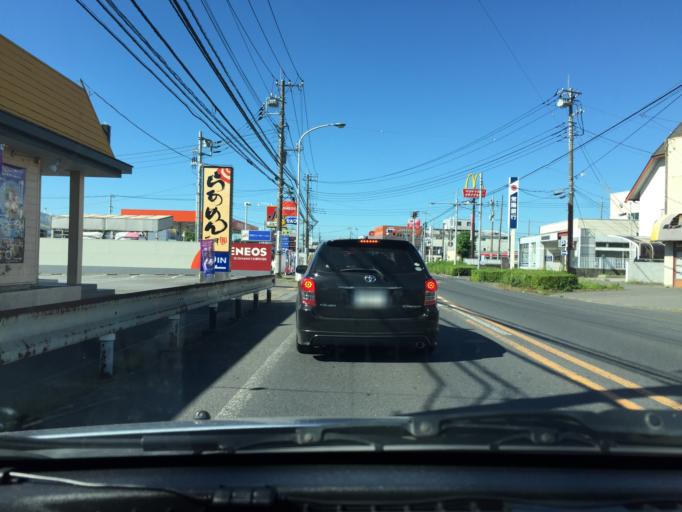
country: JP
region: Ibaraki
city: Naka
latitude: 36.0661
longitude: 140.1837
